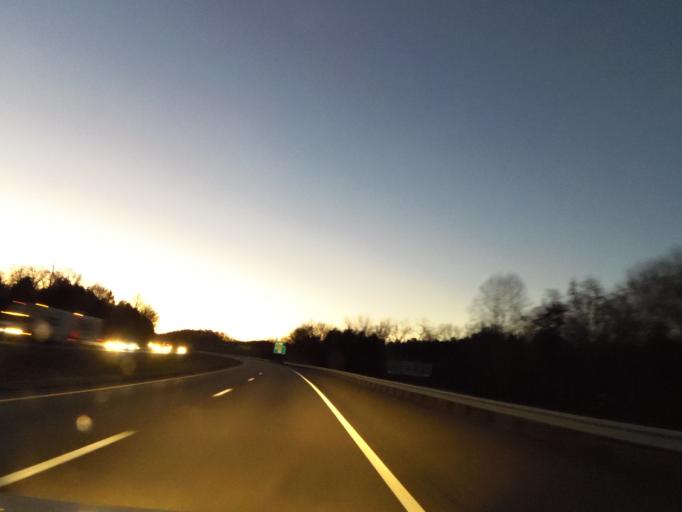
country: US
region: Tennessee
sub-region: Cocke County
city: Newport
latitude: 35.9688
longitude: -83.2277
